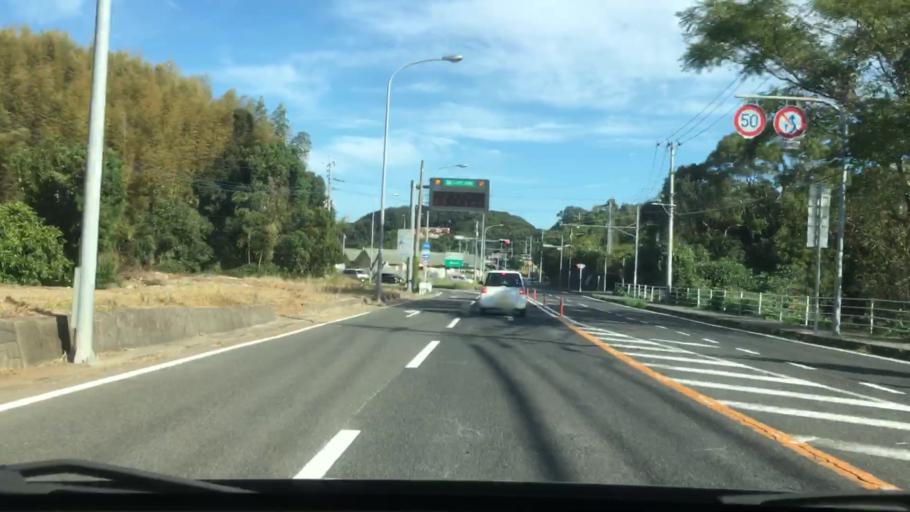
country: JP
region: Nagasaki
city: Sasebo
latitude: 33.0634
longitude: 129.7643
